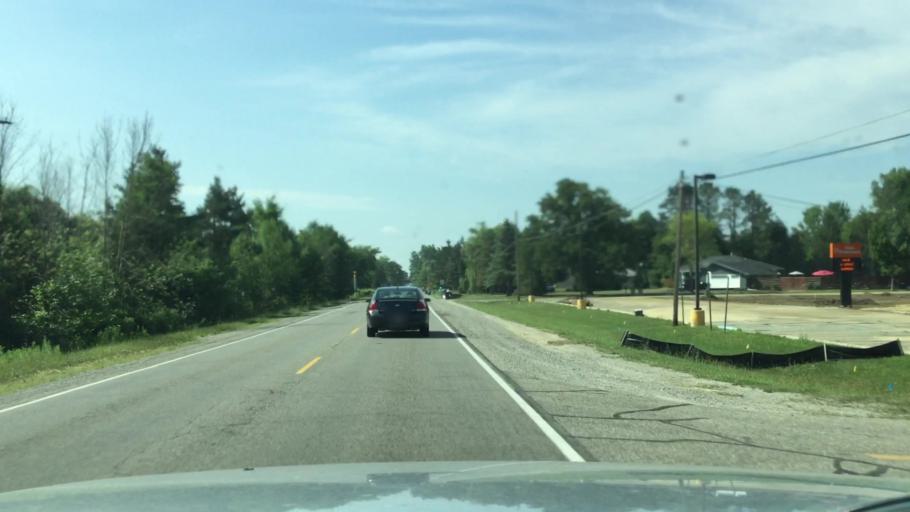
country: US
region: Michigan
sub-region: Genesee County
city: Flushing
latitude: 43.0939
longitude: -83.8136
